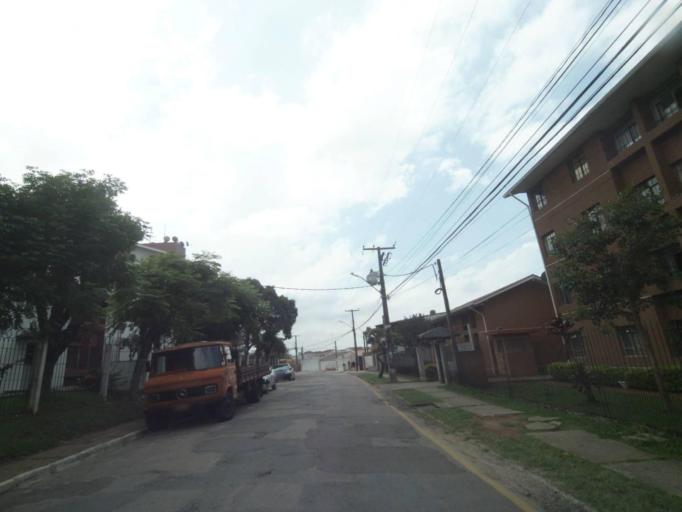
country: BR
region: Parana
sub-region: Curitiba
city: Curitiba
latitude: -25.4835
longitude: -49.3492
